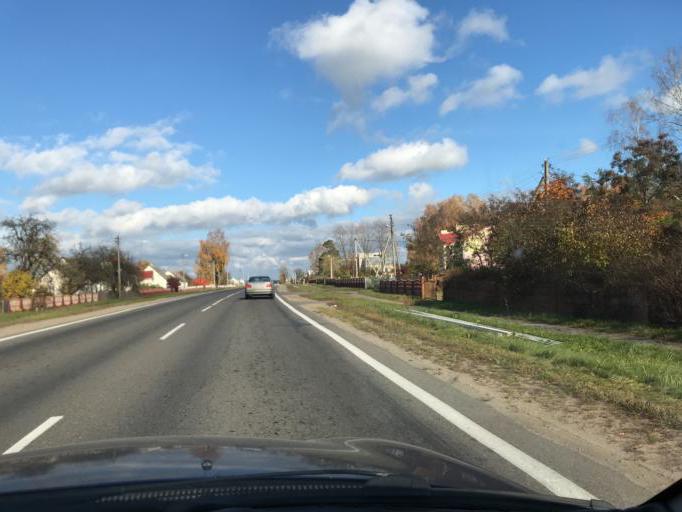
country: LT
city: Salcininkai
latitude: 54.2405
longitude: 25.3549
